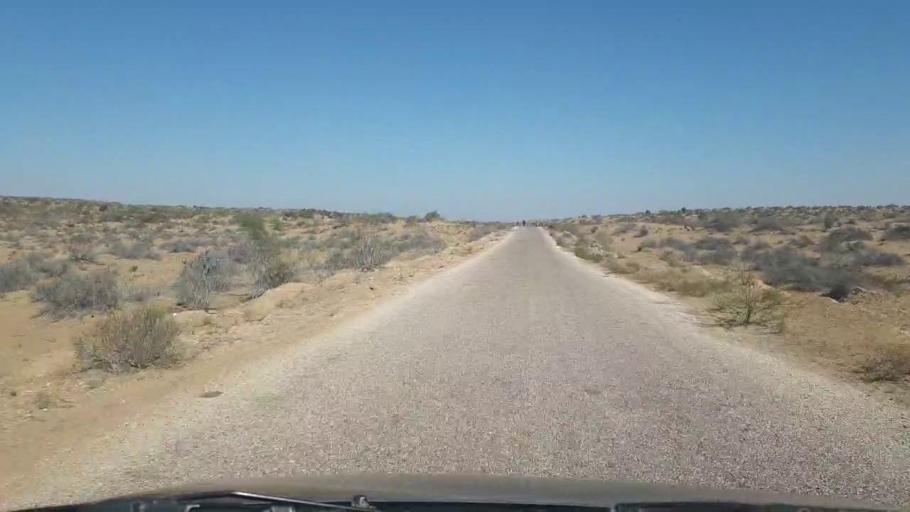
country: PK
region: Sindh
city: Bozdar
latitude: 27.0005
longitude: 68.8630
